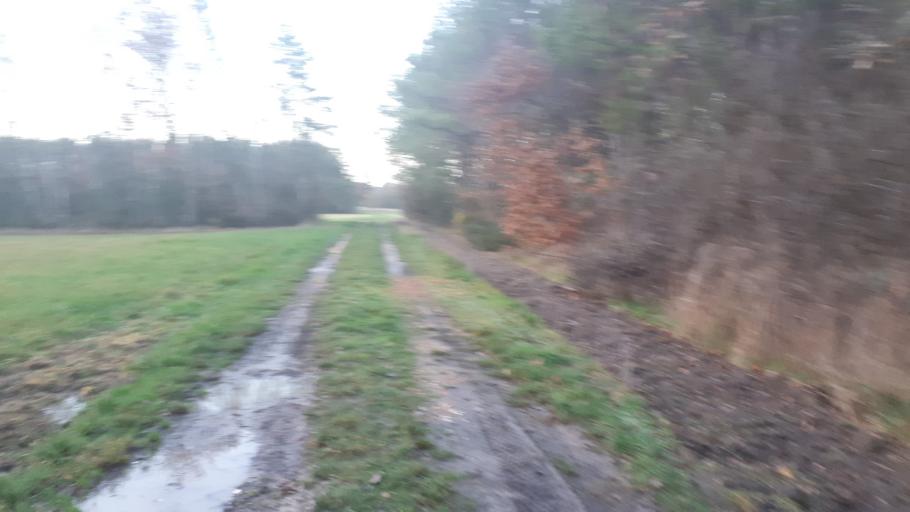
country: FR
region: Centre
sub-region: Departement du Loir-et-Cher
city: Saint-Romain-sur-Cher
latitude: 47.3481
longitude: 1.3997
